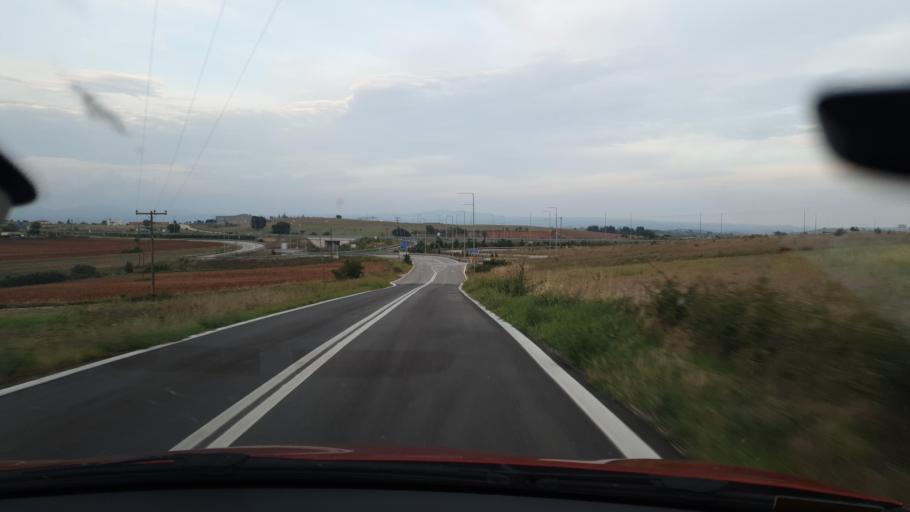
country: GR
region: Central Macedonia
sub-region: Nomos Kilkis
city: Kristoni
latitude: 40.9559
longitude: 22.8438
